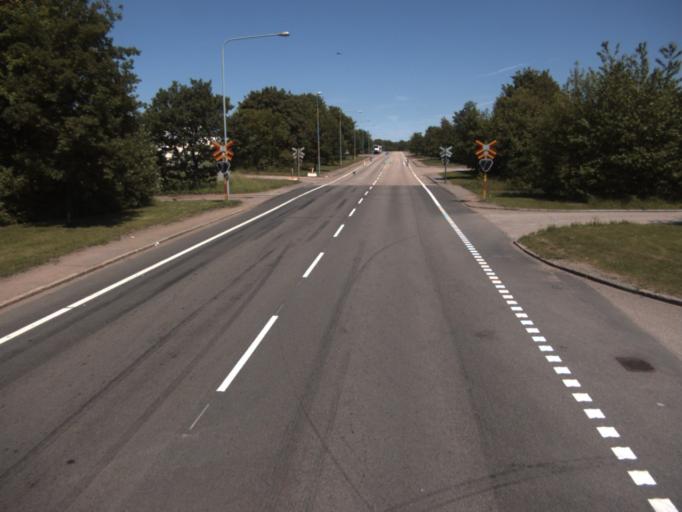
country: SE
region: Skane
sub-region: Helsingborg
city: Gantofta
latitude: 56.0117
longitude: 12.7692
